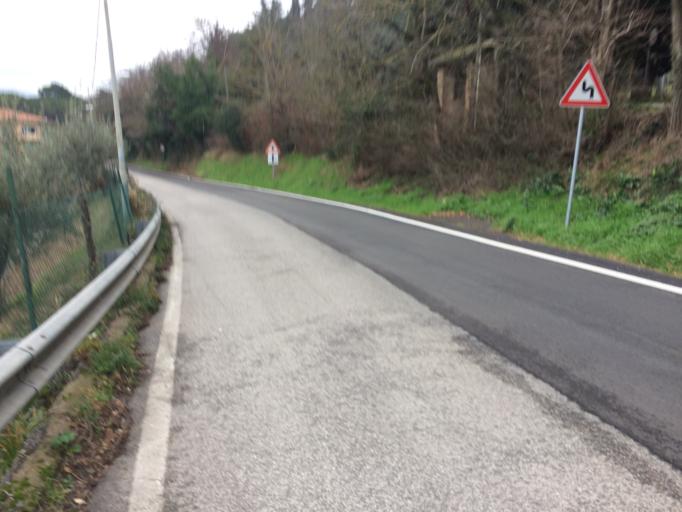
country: IT
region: Umbria
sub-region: Provincia di Perugia
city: Perugia
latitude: 43.1027
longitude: 12.4014
